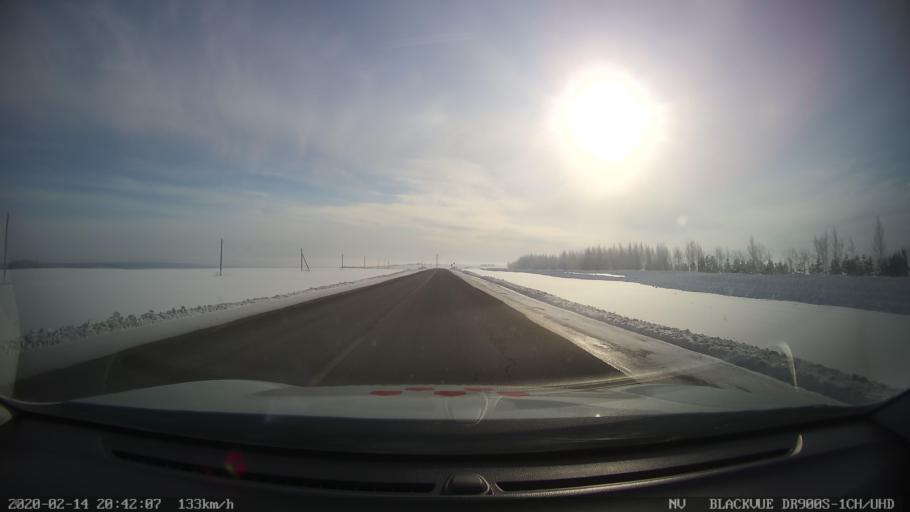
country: RU
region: Tatarstan
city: Kuybyshevskiy Zaton
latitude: 55.3207
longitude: 49.1367
